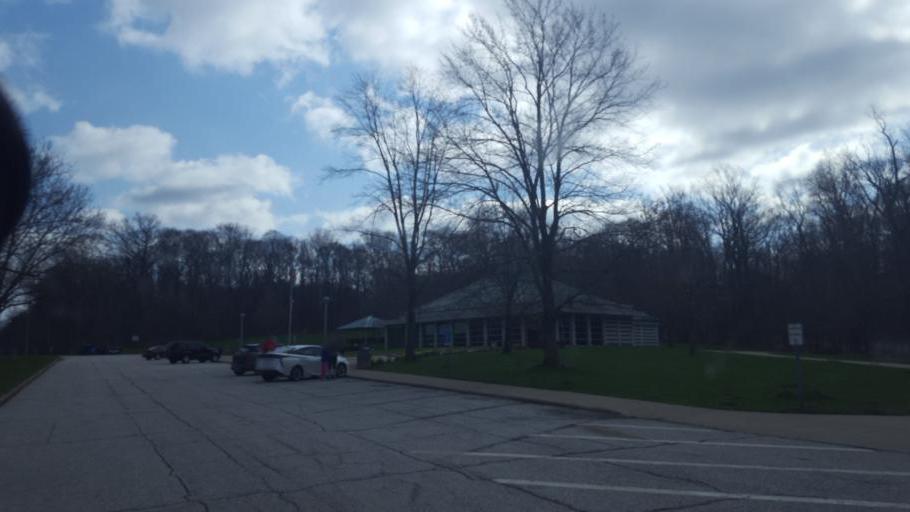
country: US
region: Ohio
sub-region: Summit County
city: Richfield
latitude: 41.2080
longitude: -81.6692
